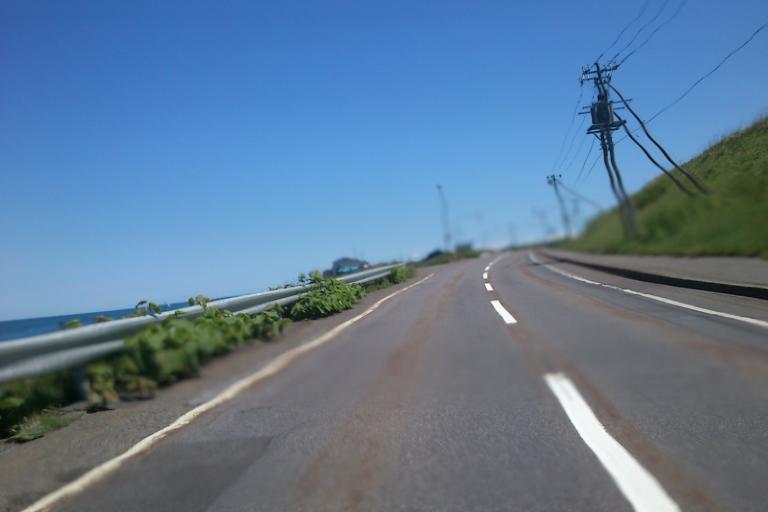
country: JP
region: Hokkaido
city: Rumoi
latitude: 43.8449
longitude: 141.5019
